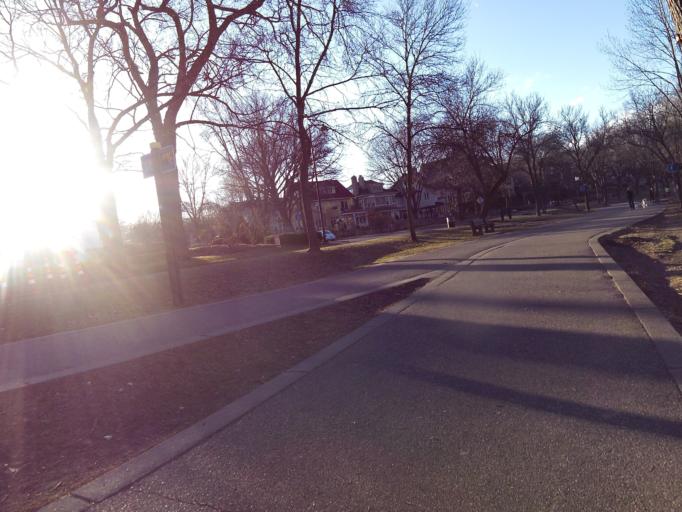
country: US
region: Minnesota
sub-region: Hennepin County
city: Richfield
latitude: 44.9178
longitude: -93.3135
